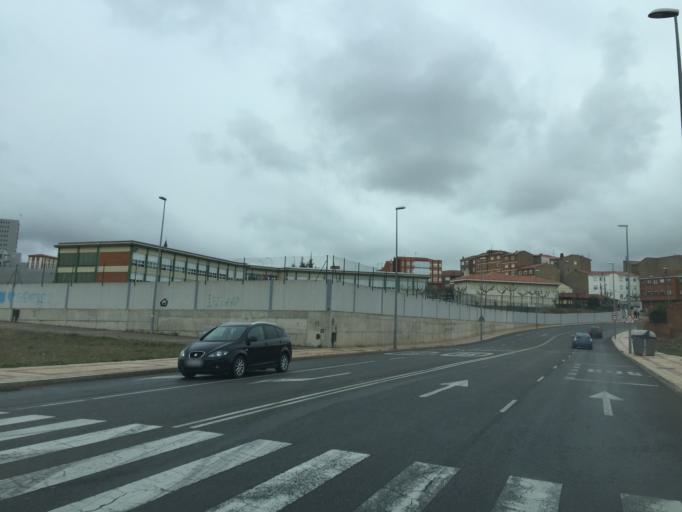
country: ES
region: Castille and Leon
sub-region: Provincia de Leon
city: Leon
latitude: 42.6145
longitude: -5.5724
